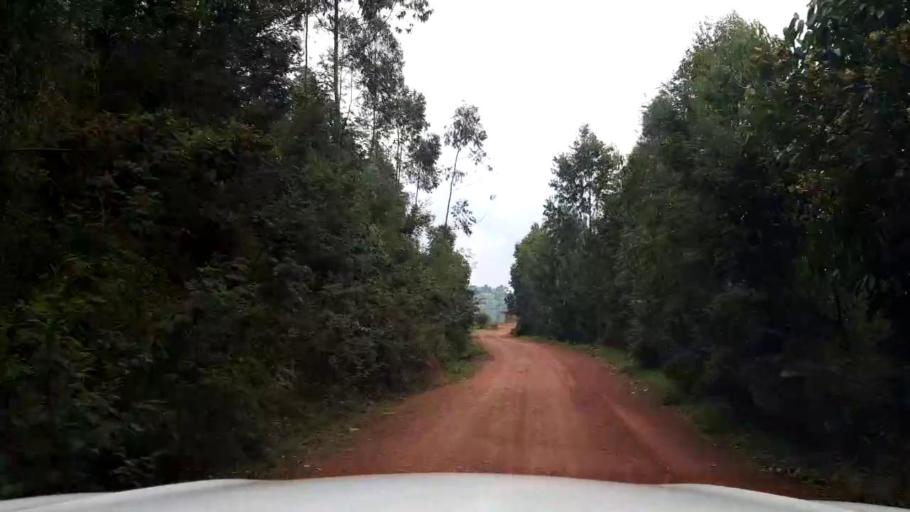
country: RW
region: Northern Province
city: Byumba
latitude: -1.4861
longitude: 29.9166
